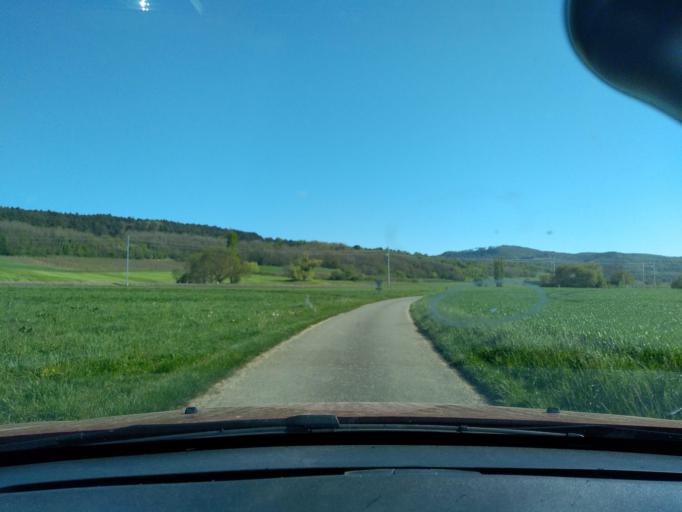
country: FR
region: Franche-Comte
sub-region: Departement du Jura
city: Montmorot
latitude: 46.6168
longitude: 5.4819
